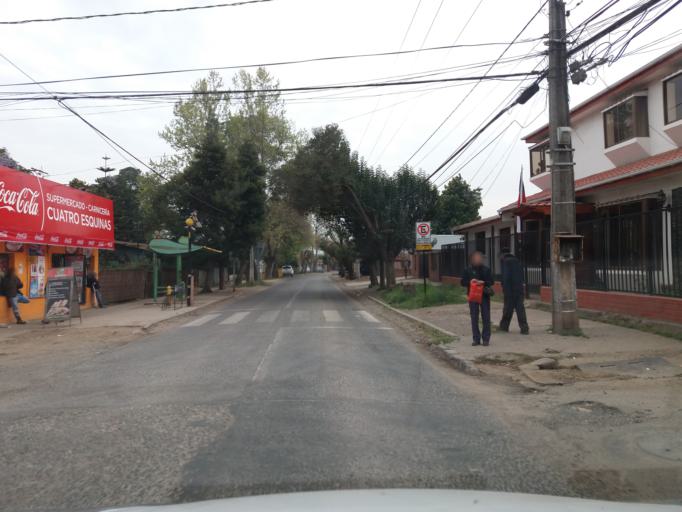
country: CL
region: Valparaiso
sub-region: Provincia de Quillota
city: Hacienda La Calera
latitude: -32.8125
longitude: -71.1401
